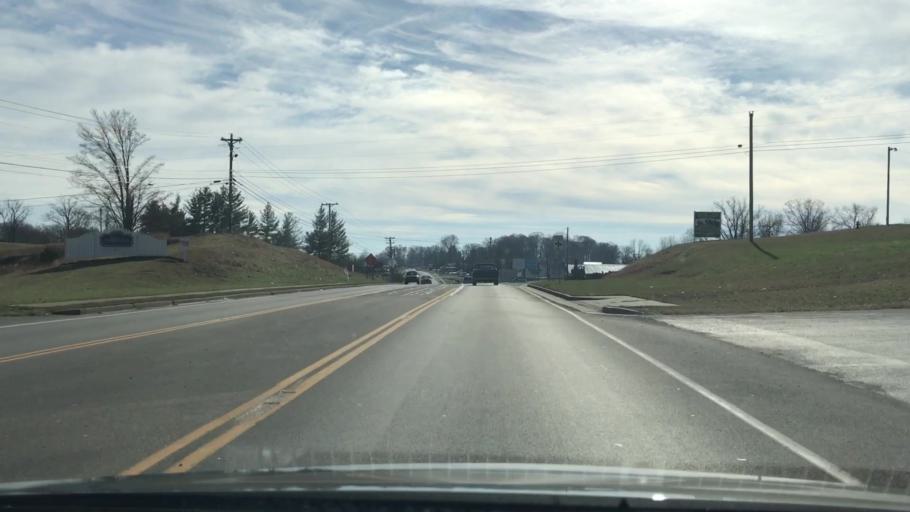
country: US
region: Kentucky
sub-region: Monroe County
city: Tompkinsville
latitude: 36.7235
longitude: -85.6875
